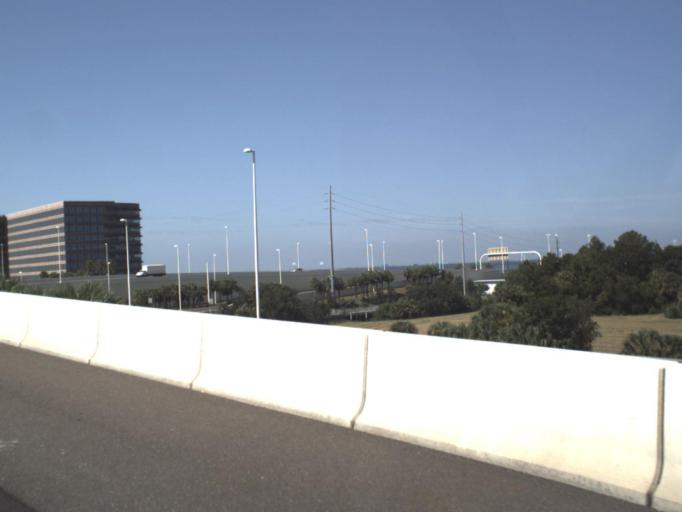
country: US
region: Florida
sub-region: Hillsborough County
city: Town 'n' Country
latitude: 27.9698
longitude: -82.5474
